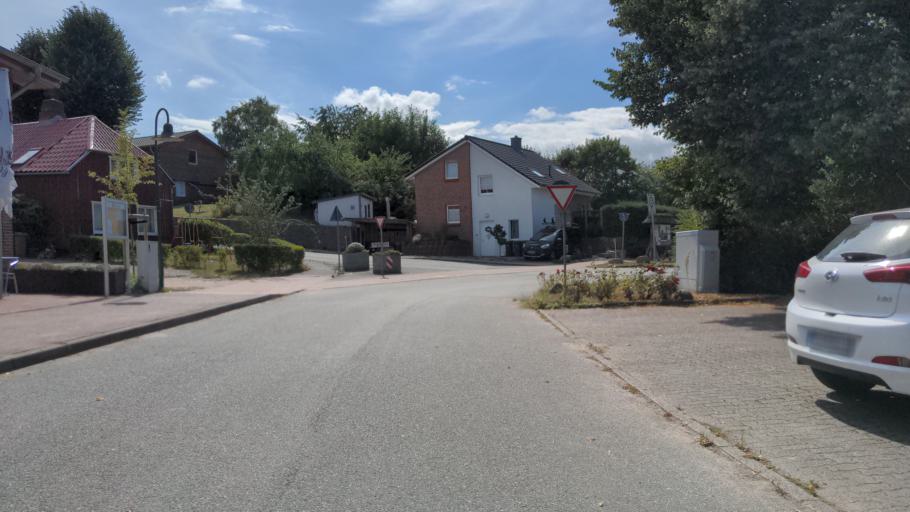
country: DE
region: Schleswig-Holstein
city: Grebin
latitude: 54.1980
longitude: 10.4943
